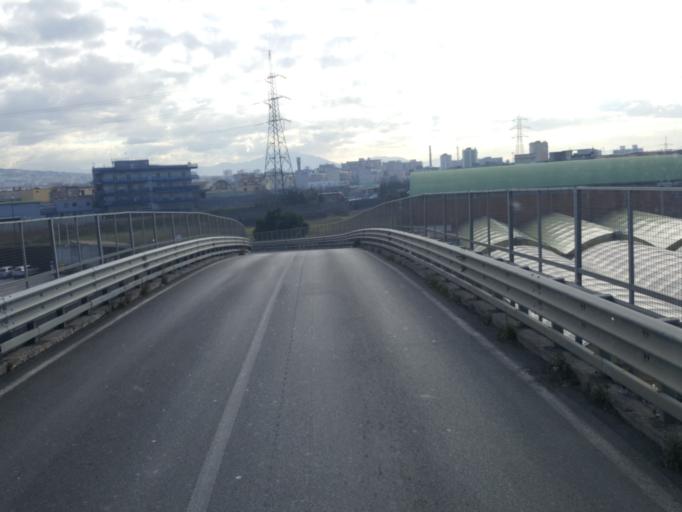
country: IT
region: Campania
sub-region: Provincia di Napoli
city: San Giorgio a Cremano
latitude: 40.8480
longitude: 14.3109
